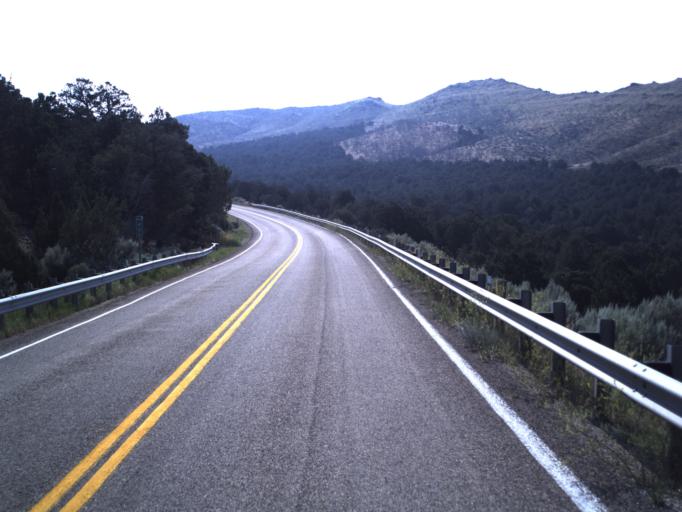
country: US
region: Utah
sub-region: Daggett County
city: Manila
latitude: 40.9535
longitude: -109.4689
